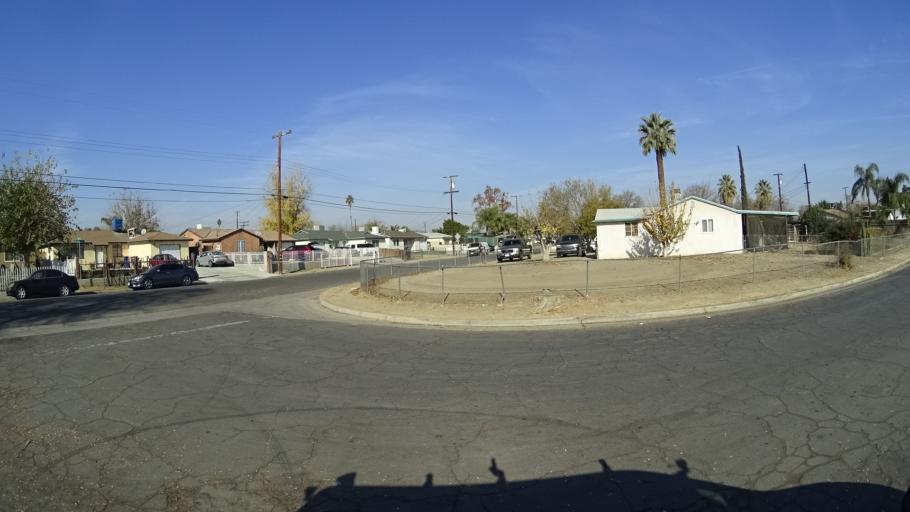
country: US
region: California
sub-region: Kern County
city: Bakersfield
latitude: 35.3265
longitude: -119.0150
